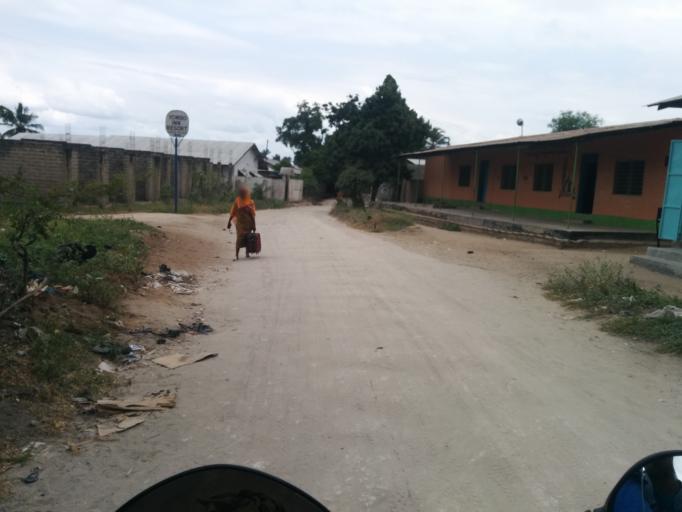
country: TZ
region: Dar es Salaam
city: Dar es Salaam
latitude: -6.8761
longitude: 39.2466
